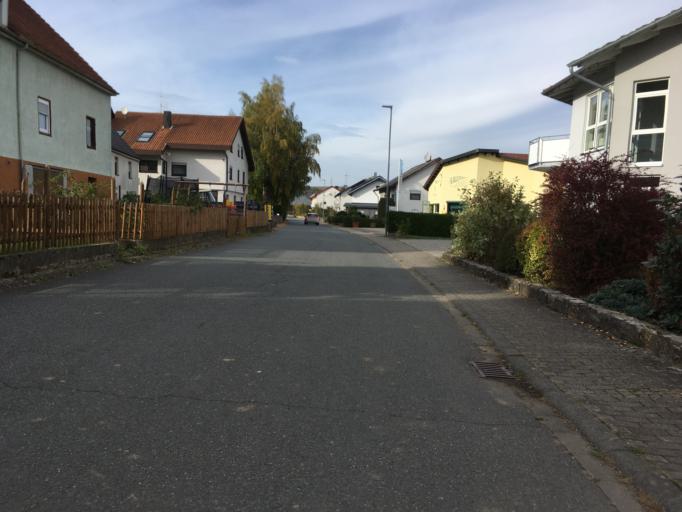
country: DE
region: Baden-Wuerttemberg
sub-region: Karlsruhe Region
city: Rosenberg
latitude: 49.5203
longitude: 9.4400
